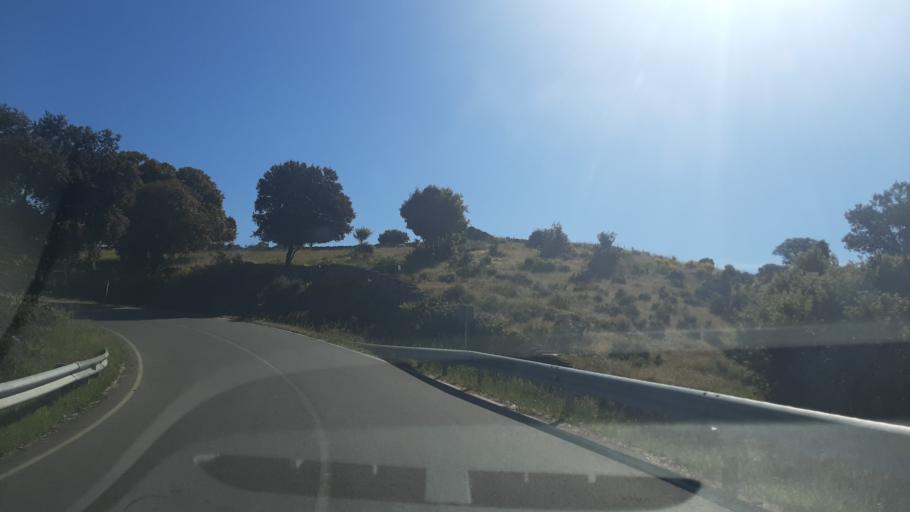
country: ES
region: Castille and Leon
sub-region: Provincia de Salamanca
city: Salvatierra de Tormes
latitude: 40.5528
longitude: -5.5885
